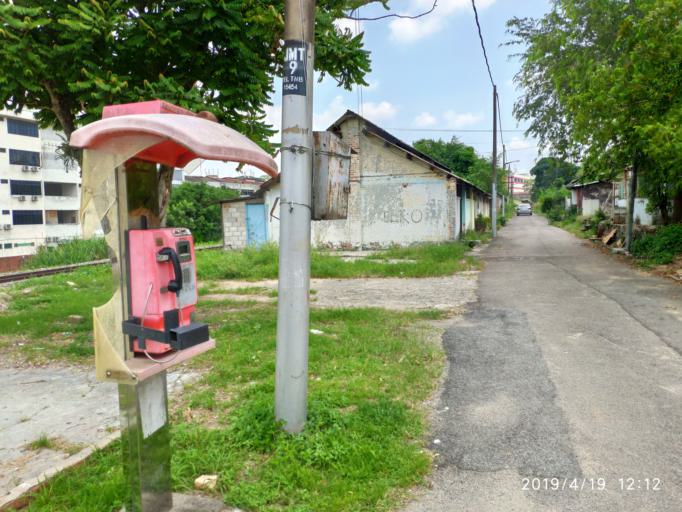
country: MY
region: Johor
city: Johor Bahru
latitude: 1.4701
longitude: 103.7591
